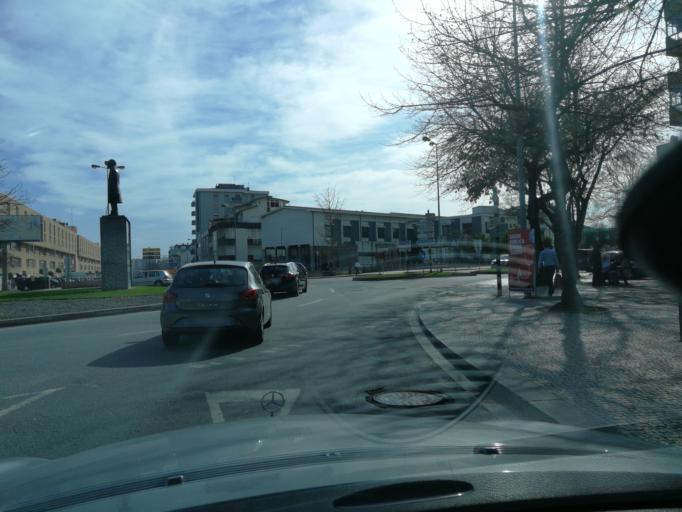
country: PT
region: Braga
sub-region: Vila Nova de Famalicao
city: Vila Nova de Famalicao
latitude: 41.4146
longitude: -8.5184
